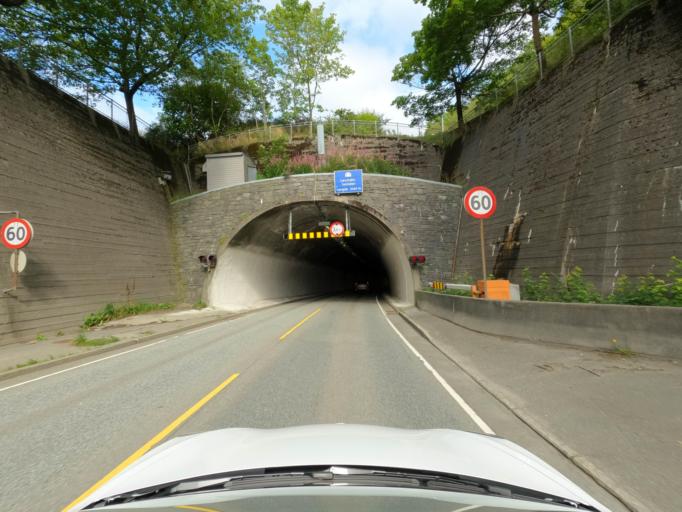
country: NO
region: Hordaland
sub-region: Bergen
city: Bergen
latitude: 60.3649
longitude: 5.2978
